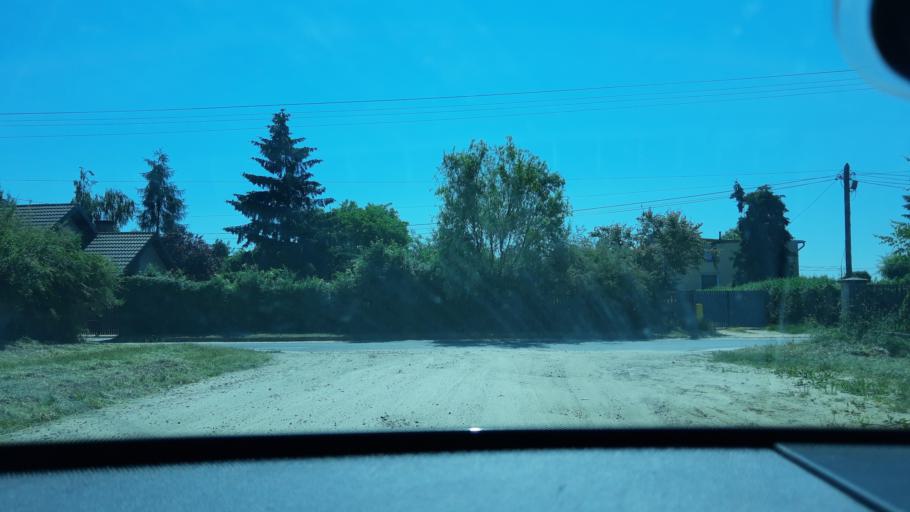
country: PL
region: Lodz Voivodeship
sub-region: Powiat sieradzki
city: Sieradz
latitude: 51.5843
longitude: 18.7348
